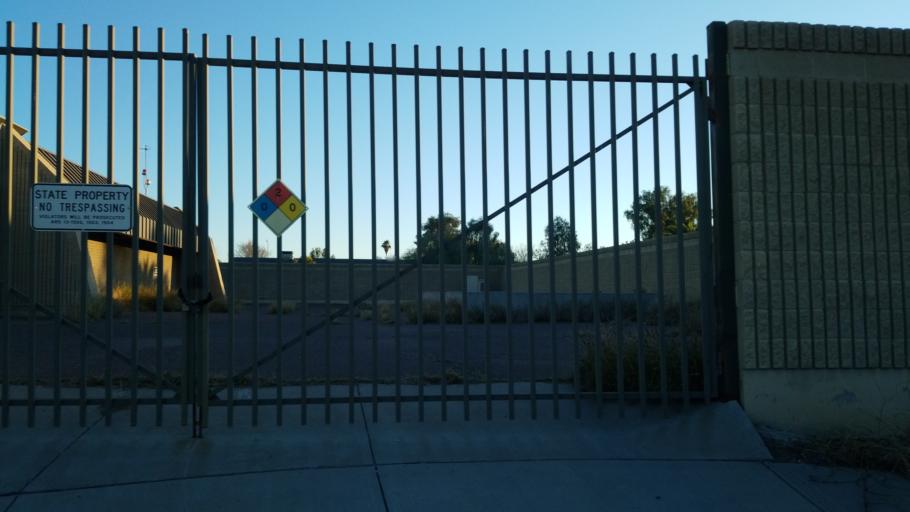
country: US
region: Arizona
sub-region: Maricopa County
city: Paradise Valley
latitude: 33.5944
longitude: -112.0107
